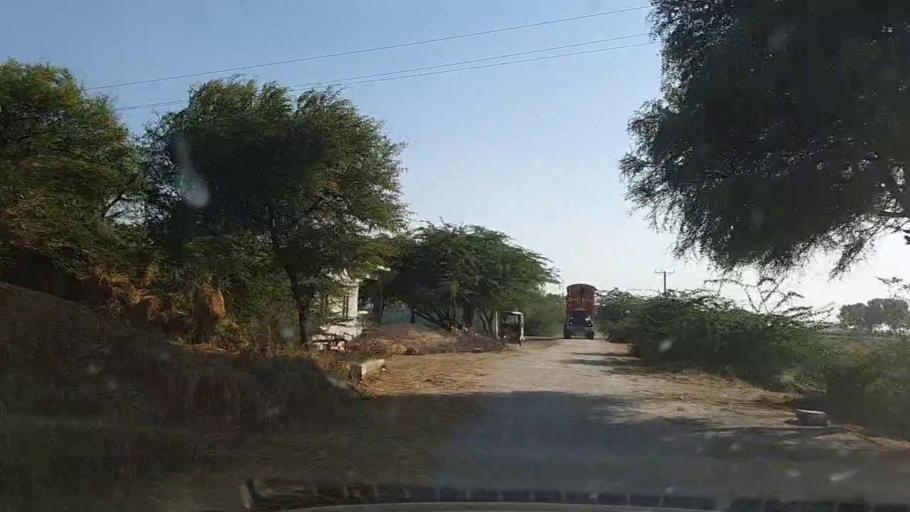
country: PK
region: Sindh
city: Daro Mehar
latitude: 24.6474
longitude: 68.0751
